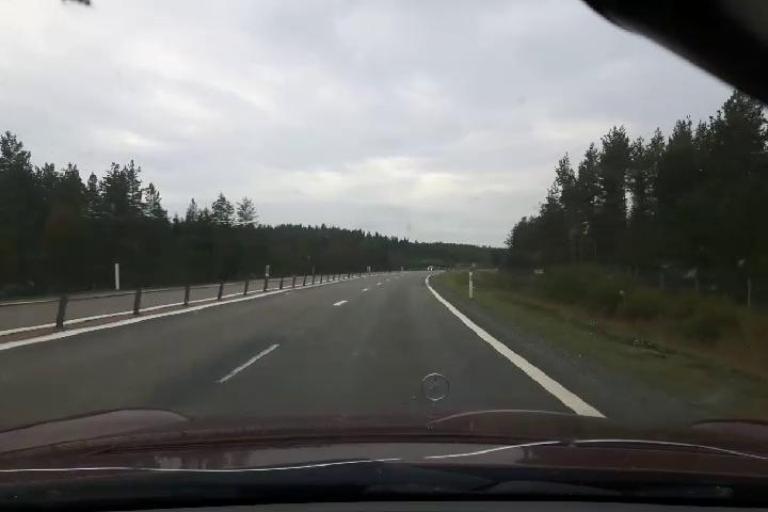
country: SE
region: Vaesternorrland
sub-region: Haernoesands Kommun
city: Haernoesand
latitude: 62.7219
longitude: 17.9201
